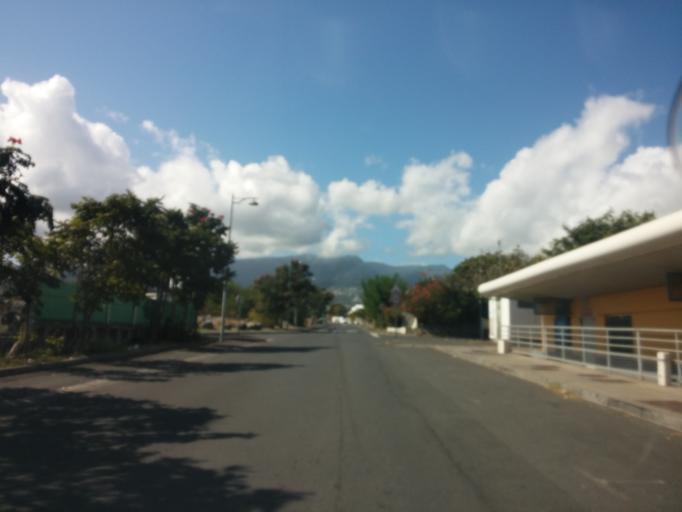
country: RE
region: Reunion
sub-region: Reunion
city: Le Port
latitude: -20.9525
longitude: 55.3020
